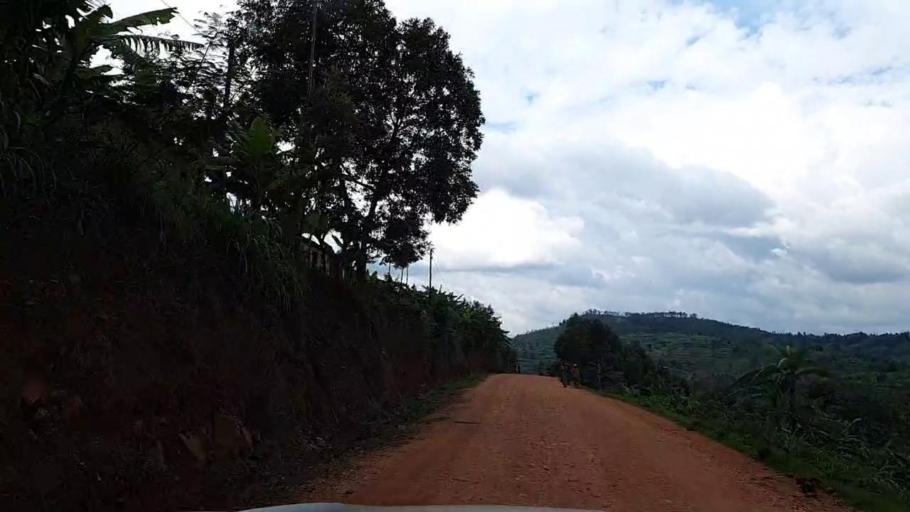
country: RW
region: Southern Province
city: Nyanza
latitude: -2.4148
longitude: 29.6701
